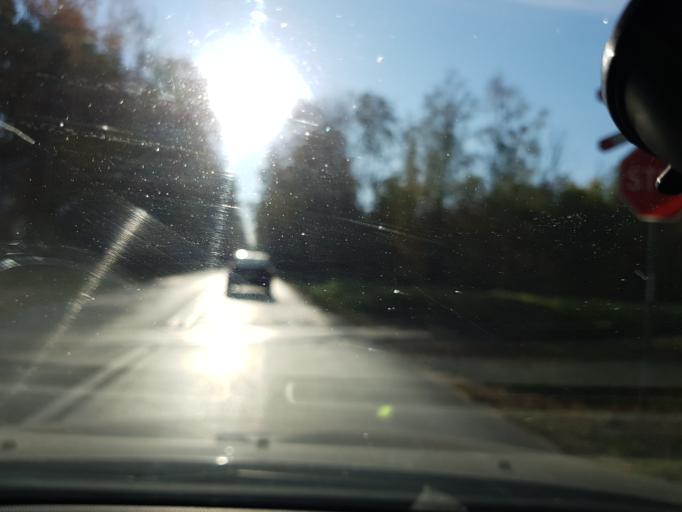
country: PL
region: Masovian Voivodeship
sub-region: Powiat warszawski zachodni
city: Babice
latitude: 52.2701
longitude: 20.8736
